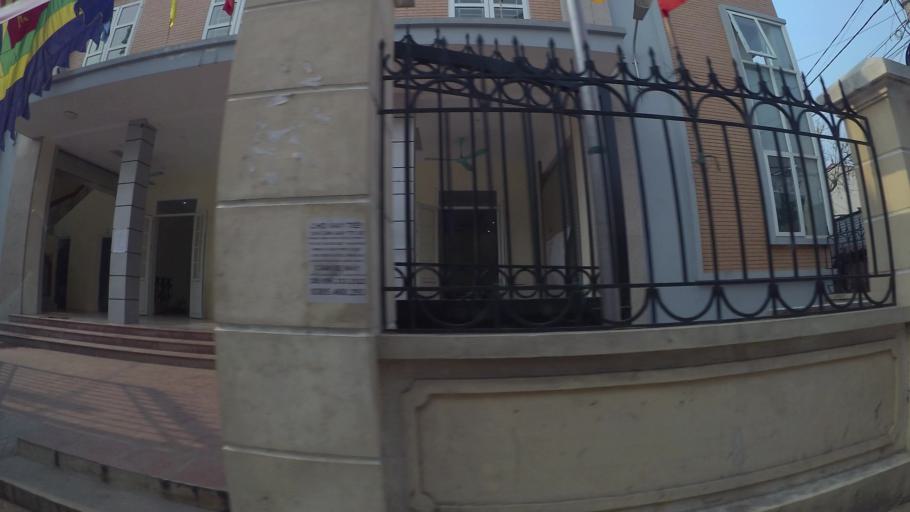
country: VN
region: Ha Noi
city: Thuong Tin
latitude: 20.8655
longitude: 105.8753
